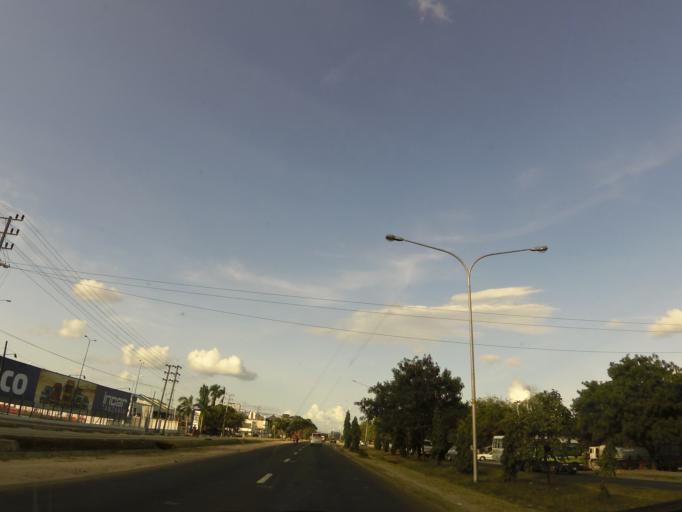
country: TZ
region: Dar es Salaam
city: Dar es Salaam
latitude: -6.8475
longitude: 39.2379
